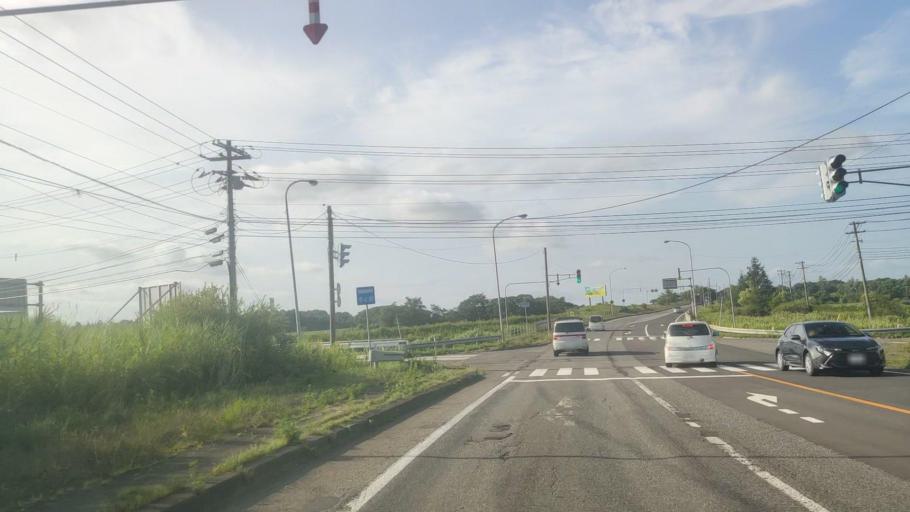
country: JP
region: Hokkaido
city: Chitose
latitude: 42.8852
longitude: 141.8122
